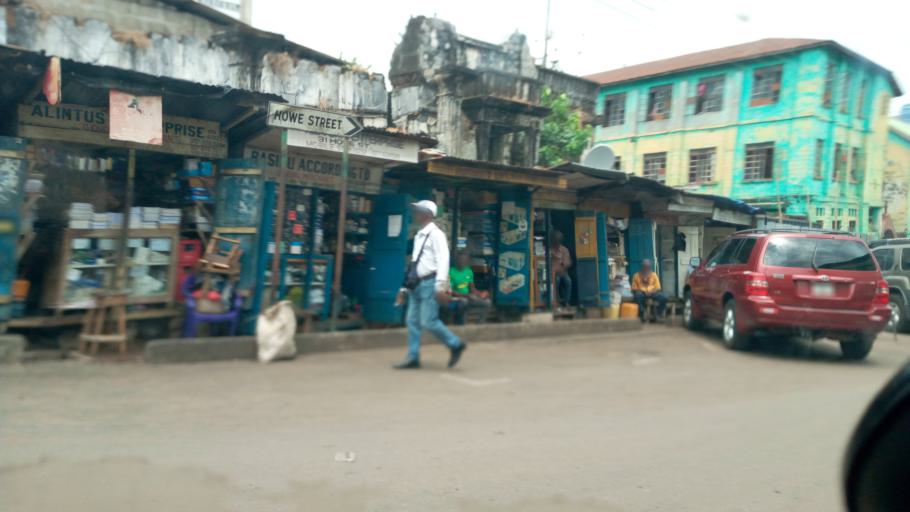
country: SL
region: Western Area
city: Freetown
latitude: 8.4879
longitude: -13.2323
